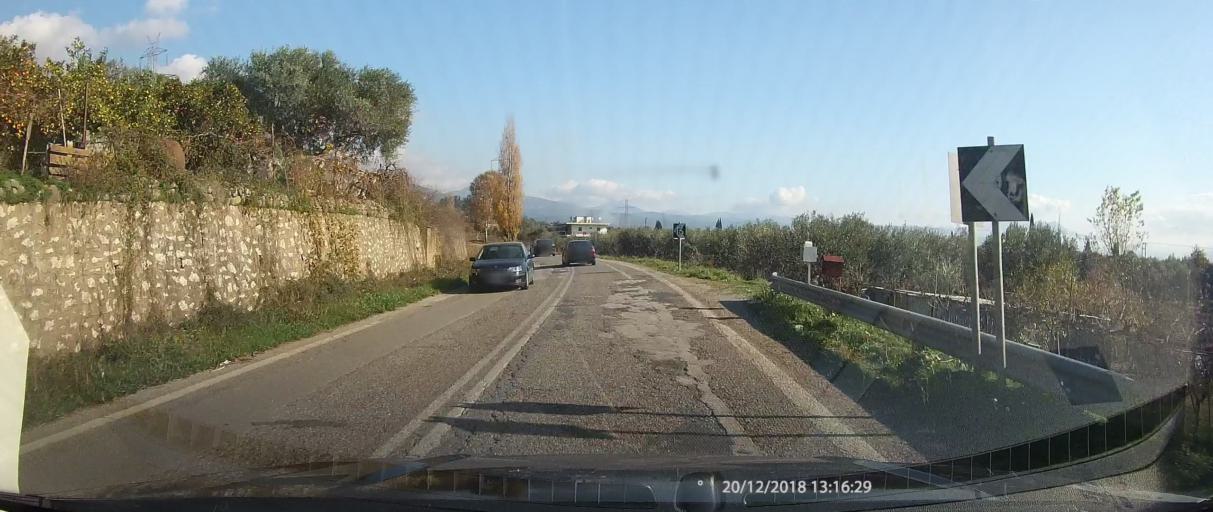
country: GR
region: West Greece
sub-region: Nomos Aitolias kai Akarnanias
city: Paravola
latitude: 38.6105
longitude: 21.5101
